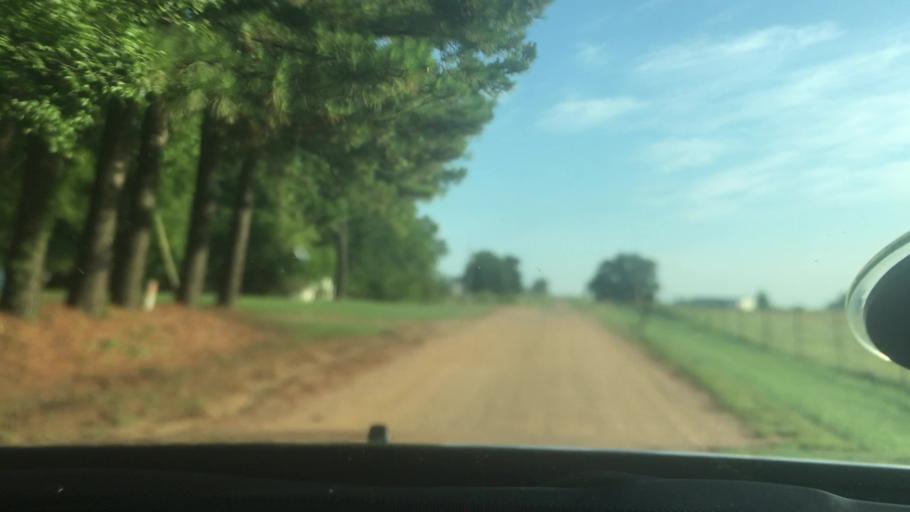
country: US
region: Oklahoma
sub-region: Pontotoc County
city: Ada
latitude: 34.8149
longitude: -96.7748
